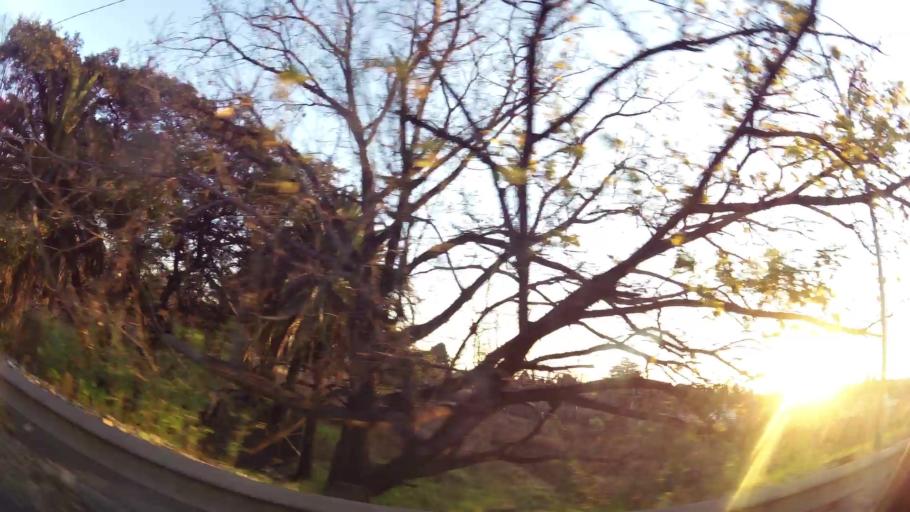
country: ZA
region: Gauteng
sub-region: Ekurhuleni Metropolitan Municipality
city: Germiston
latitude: -26.2687
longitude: 28.1653
